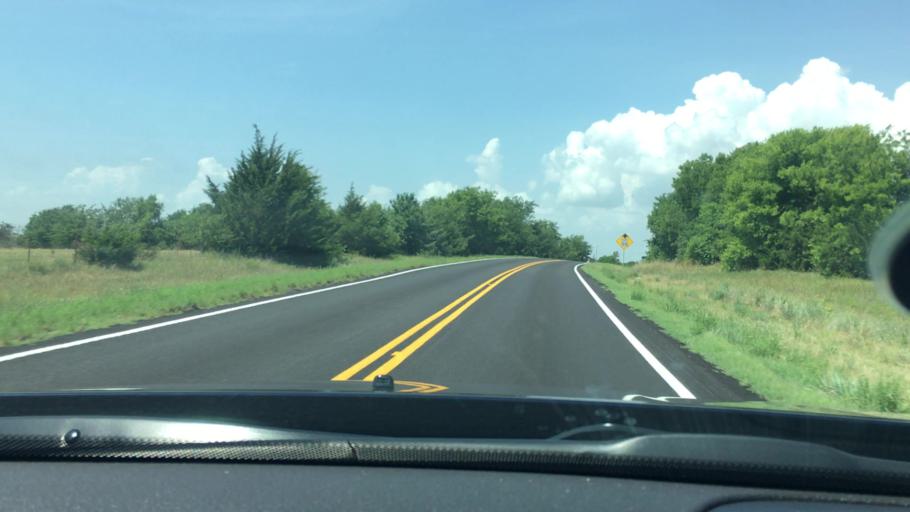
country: US
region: Oklahoma
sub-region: Marshall County
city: Kingston
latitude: 34.0868
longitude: -96.5985
